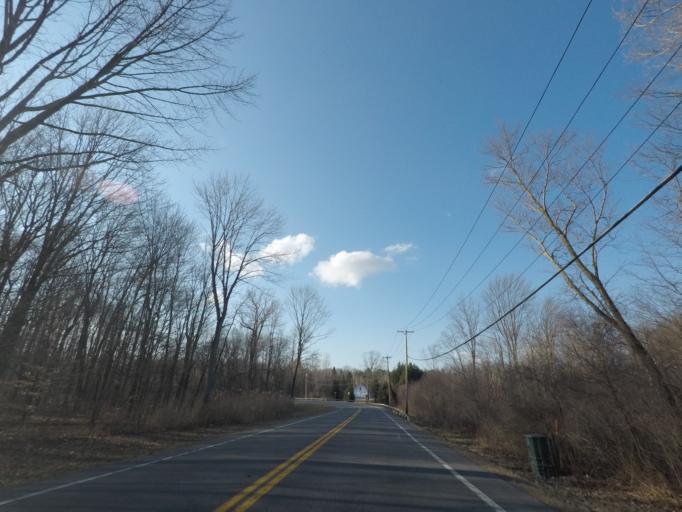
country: US
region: New York
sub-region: Schenectady County
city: Niskayuna
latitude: 42.8319
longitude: -73.7904
